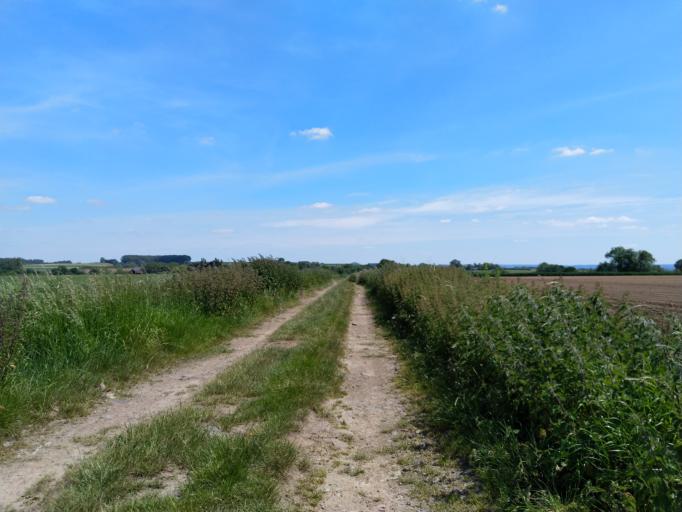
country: BE
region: Wallonia
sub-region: Province du Hainaut
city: Roeulx
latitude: 50.5023
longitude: 4.0556
